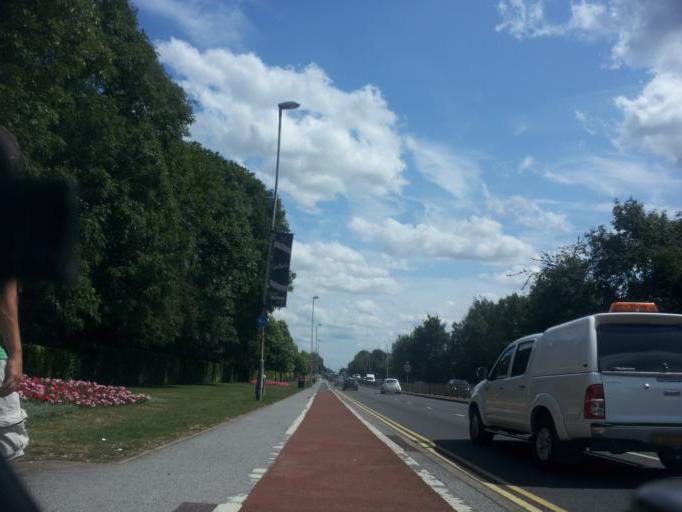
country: GB
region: England
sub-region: Kent
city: Gillingham
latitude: 51.3721
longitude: 0.5616
